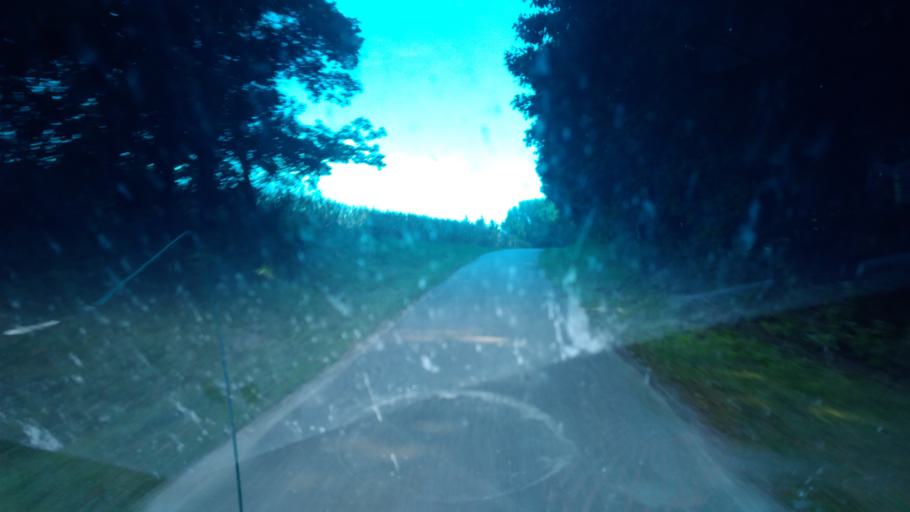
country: US
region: Ohio
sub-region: Wyandot County
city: Upper Sandusky
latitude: 40.9267
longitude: -83.2444
